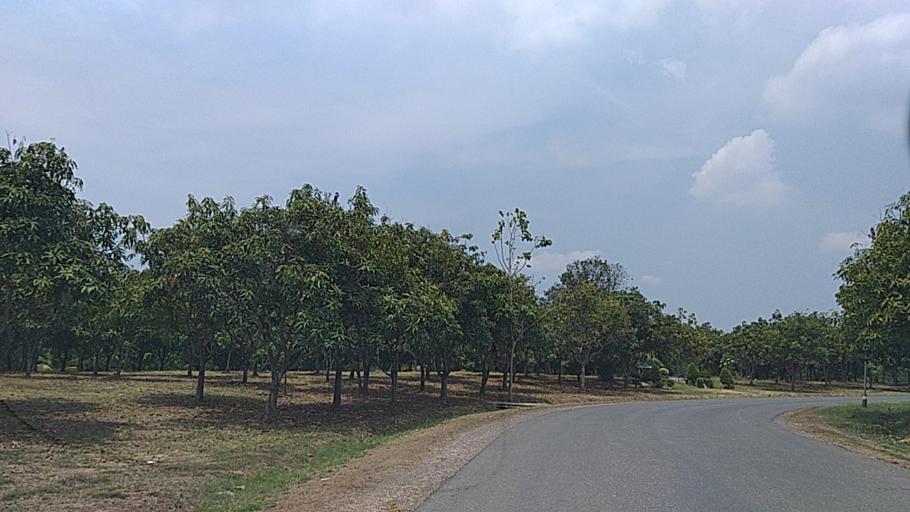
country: TH
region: Bangkok
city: Thawi Watthana
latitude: 13.7709
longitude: 100.3117
